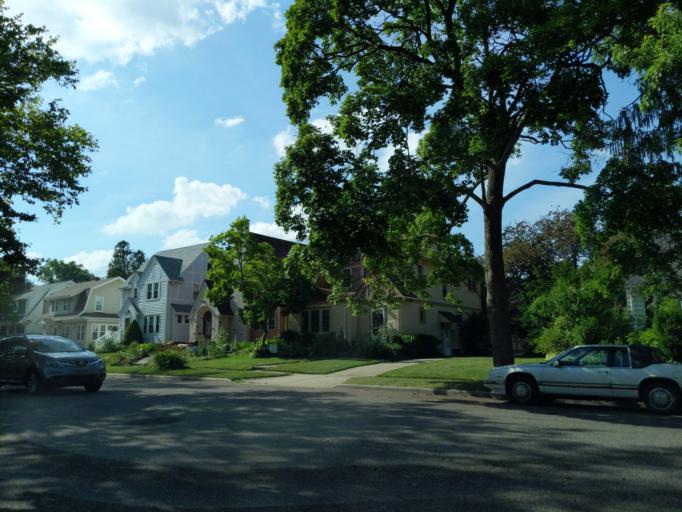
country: US
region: Michigan
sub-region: Ingham County
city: Lansing
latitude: 42.7368
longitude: -84.5742
